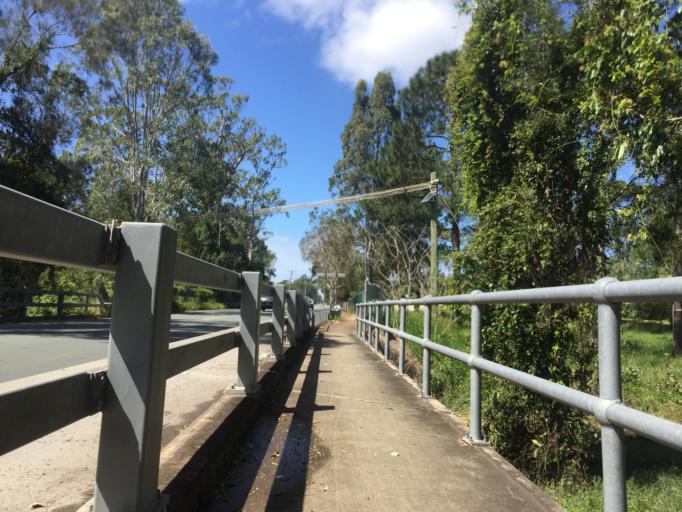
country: AU
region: Queensland
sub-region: Moreton Bay
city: Morayfield
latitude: -27.1103
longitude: 152.9325
